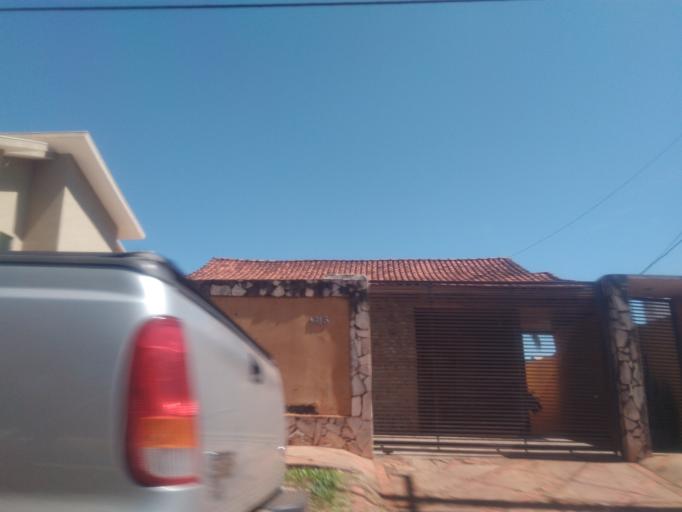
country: BR
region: Mato Grosso do Sul
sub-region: Ponta Pora
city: Ponta Pora
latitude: -22.5211
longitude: -55.7212
